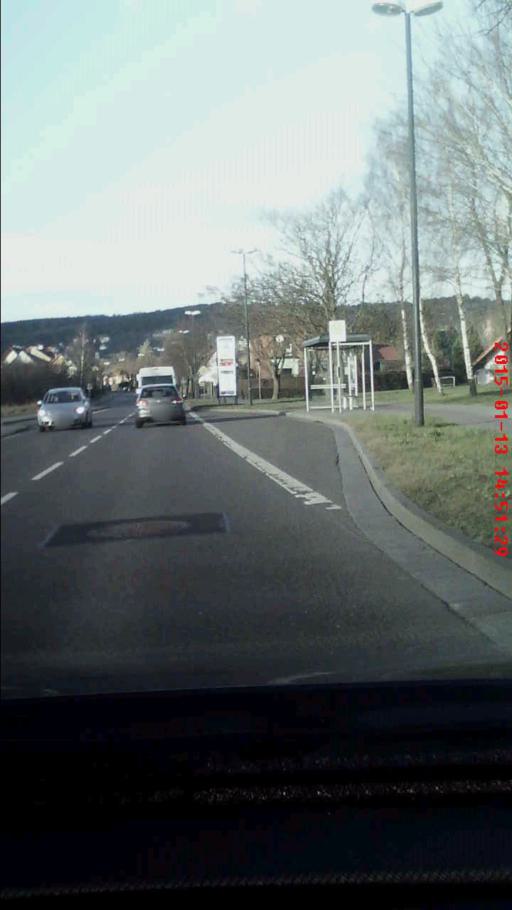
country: DE
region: Thuringia
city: Bad Frankenhausen
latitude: 51.3480
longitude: 11.1078
